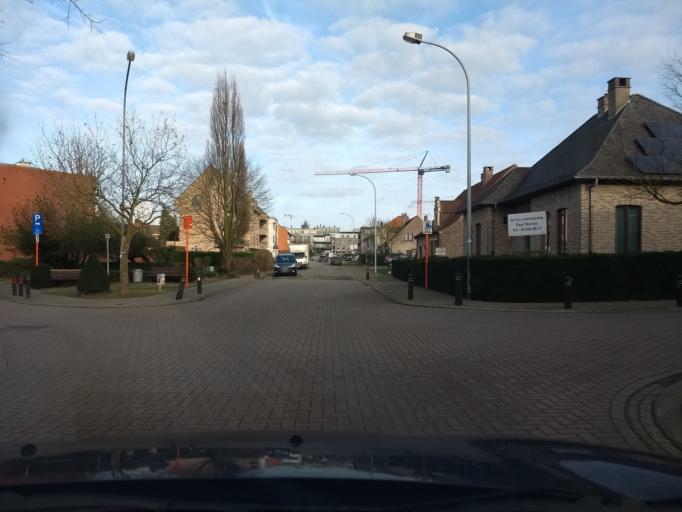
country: BE
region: Flanders
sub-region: Provincie Vlaams-Brabant
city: Halle
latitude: 50.7271
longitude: 4.2370
